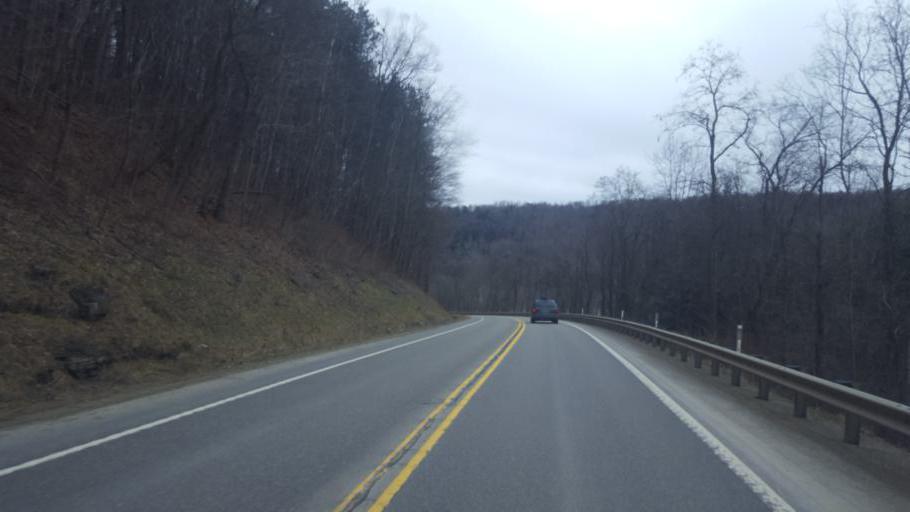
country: US
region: Pennsylvania
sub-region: Potter County
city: Coudersport
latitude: 41.7427
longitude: -78.0837
